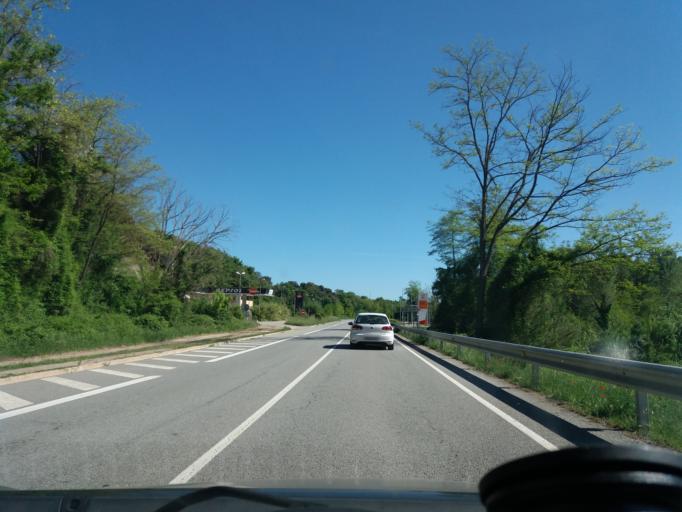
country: ES
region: Catalonia
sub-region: Provincia de Barcelona
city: Avia
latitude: 42.0621
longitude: 1.8715
